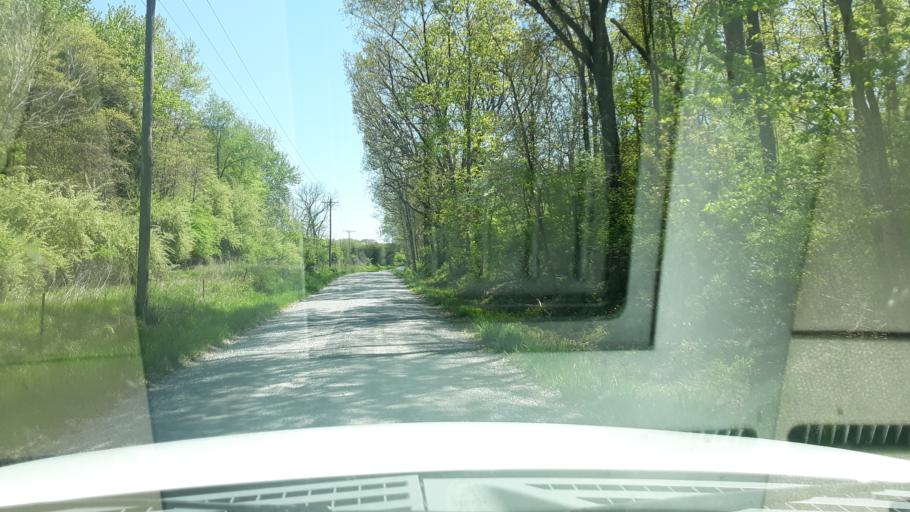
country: US
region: Illinois
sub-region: Saline County
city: Harrisburg
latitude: 37.8648
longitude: -88.6404
